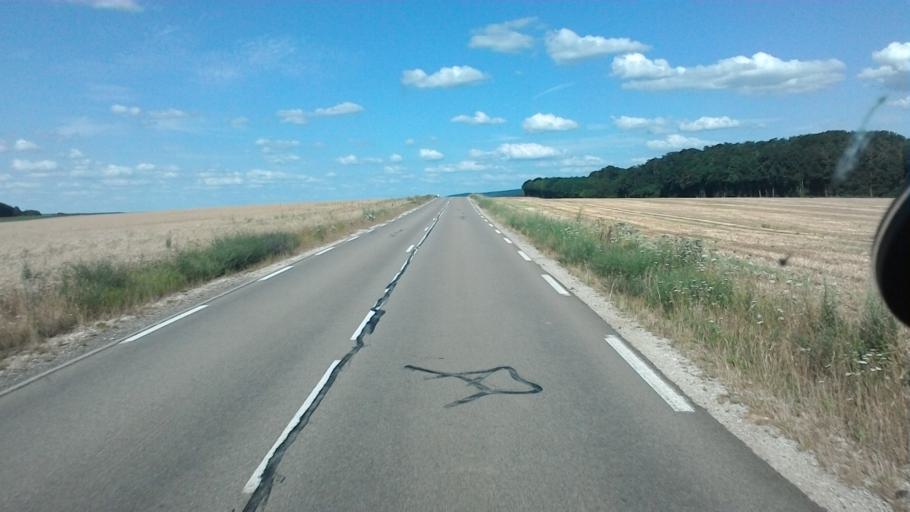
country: FR
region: Franche-Comte
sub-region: Departement de la Haute-Saone
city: Marnay
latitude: 47.3604
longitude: 5.7334
